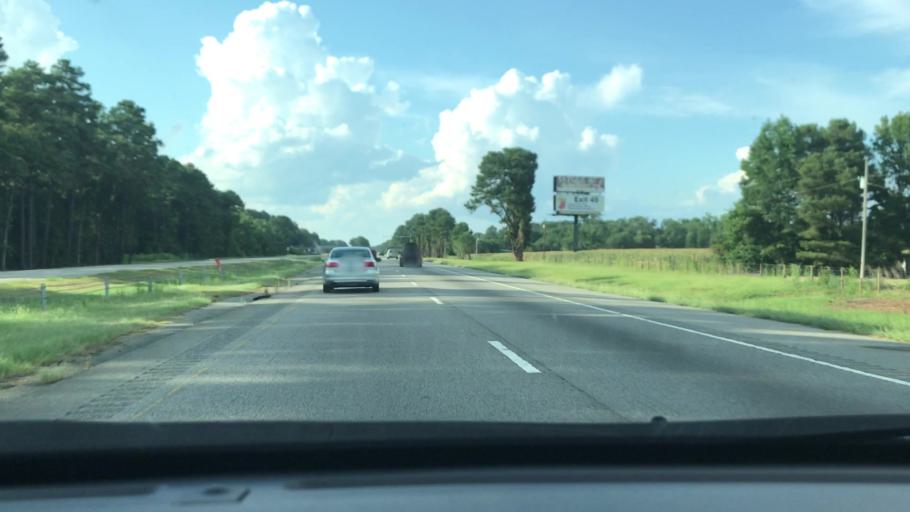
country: US
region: North Carolina
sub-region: Robeson County
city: Lumberton
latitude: 34.6952
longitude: -78.9984
